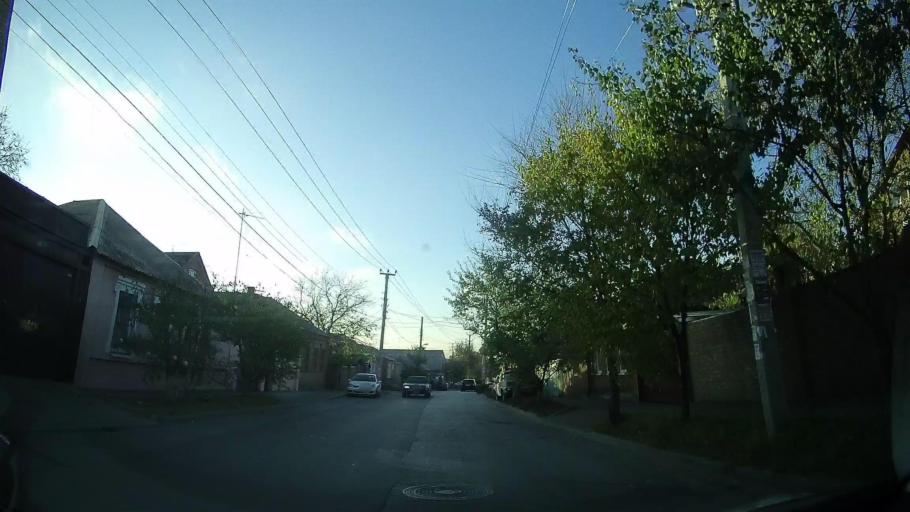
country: RU
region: Rostov
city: Severnyy
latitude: 47.2654
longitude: 39.6804
